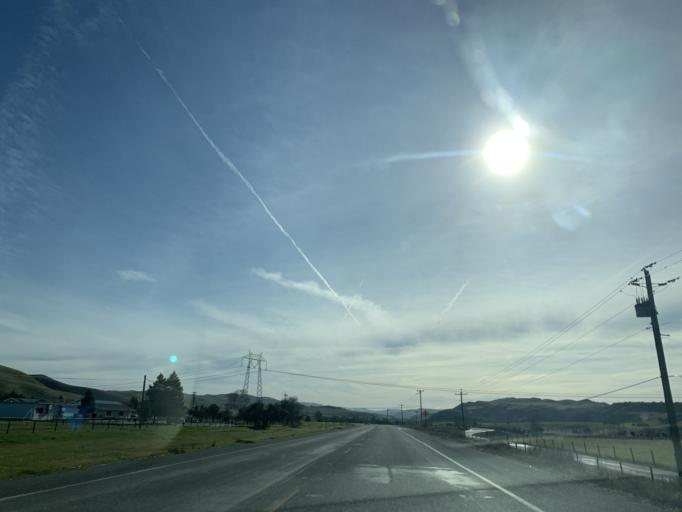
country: US
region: California
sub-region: San Benito County
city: Ridgemark
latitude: 36.8020
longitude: -121.3381
